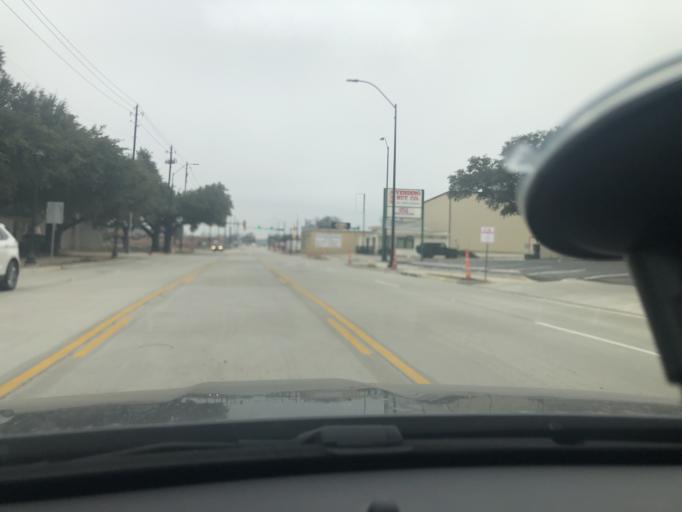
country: US
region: Texas
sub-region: Tarrant County
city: Westworth
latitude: 32.7375
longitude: -97.3700
